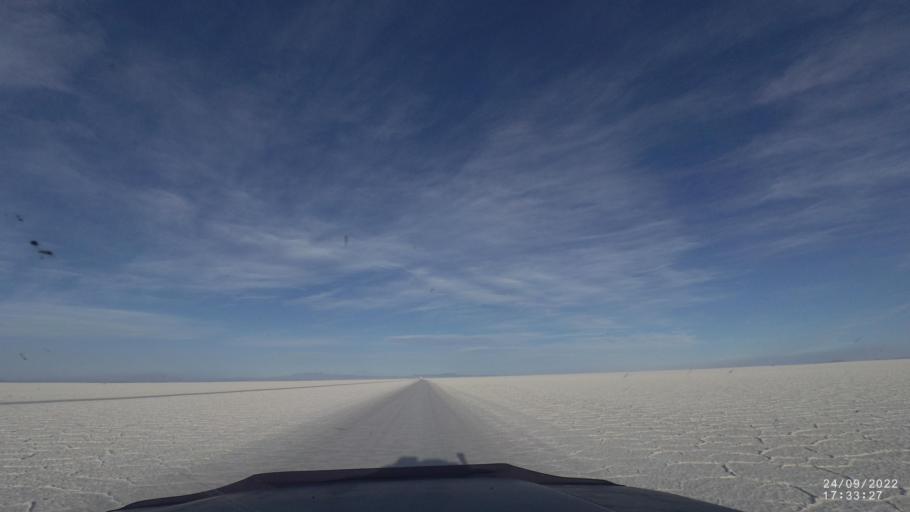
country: BO
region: Potosi
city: Colchani
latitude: -20.3199
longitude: -67.3055
